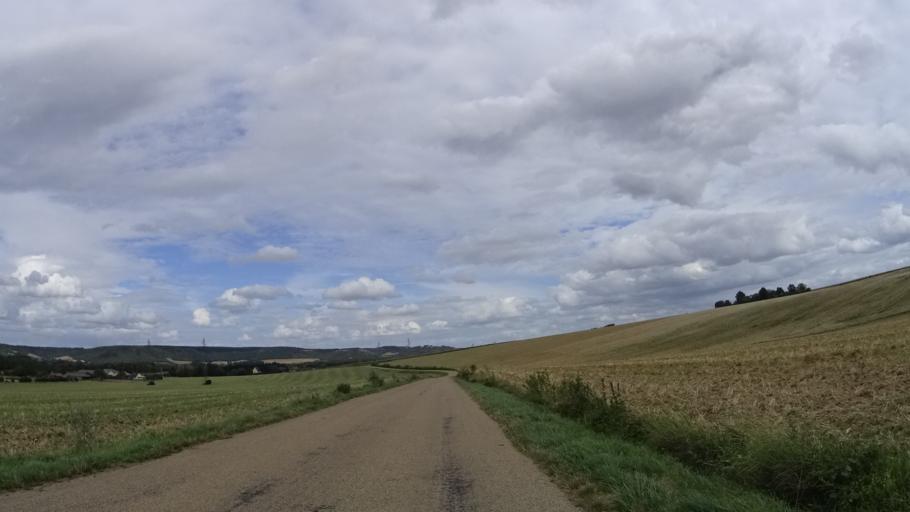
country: FR
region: Bourgogne
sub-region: Departement de l'Yonne
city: Cezy
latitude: 47.9827
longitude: 3.3178
